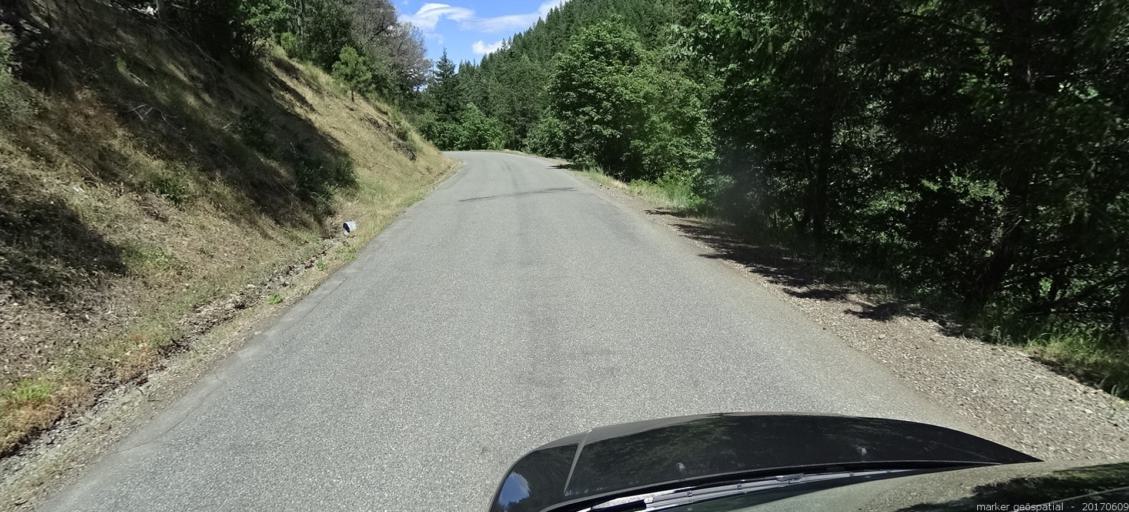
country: US
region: California
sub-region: Siskiyou County
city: Yreka
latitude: 41.4309
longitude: -122.9179
